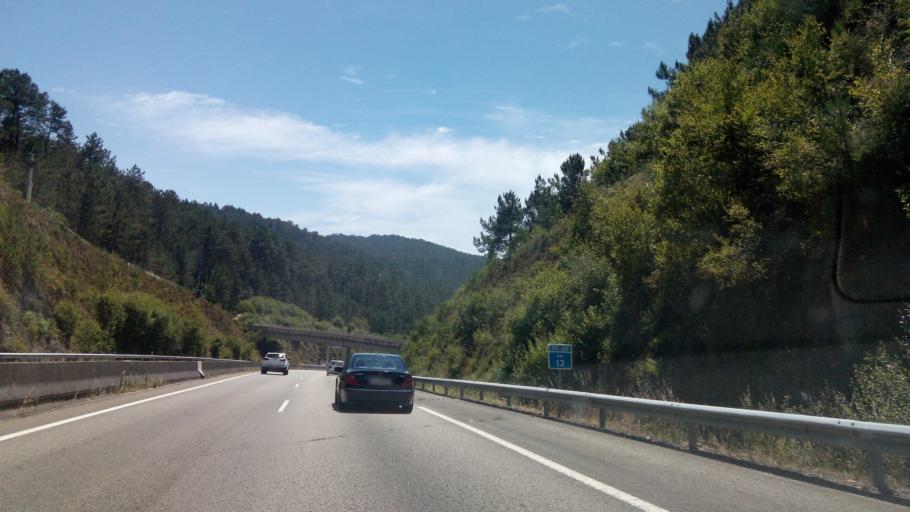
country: ES
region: Galicia
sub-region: Provincia de Pontevedra
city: Porrino
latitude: 42.1875
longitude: -8.6723
